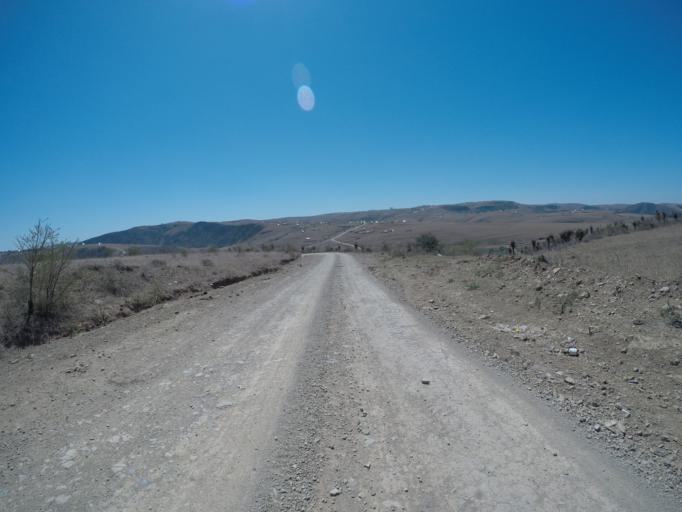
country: ZA
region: Eastern Cape
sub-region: OR Tambo District Municipality
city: Mthatha
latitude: -31.8738
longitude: 28.8723
